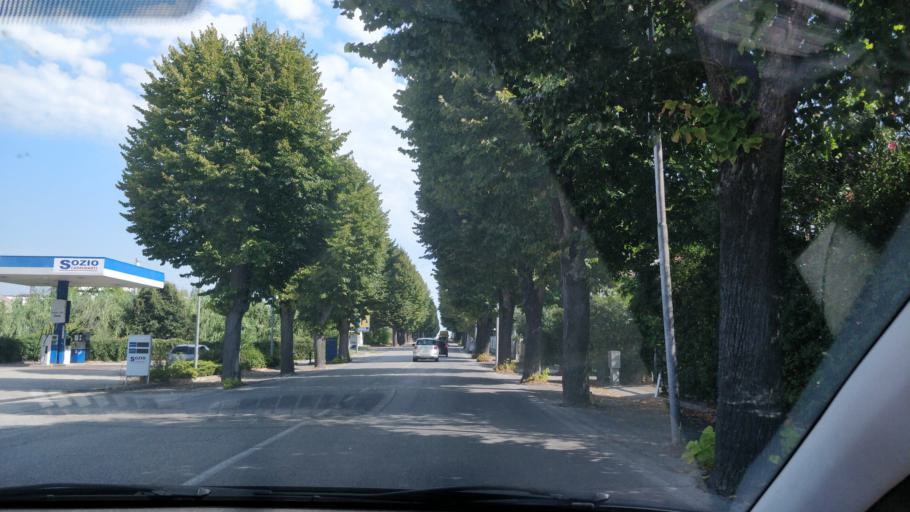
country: IT
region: Abruzzo
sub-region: Provincia di Chieti
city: Chieti
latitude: 42.3907
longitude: 14.1594
